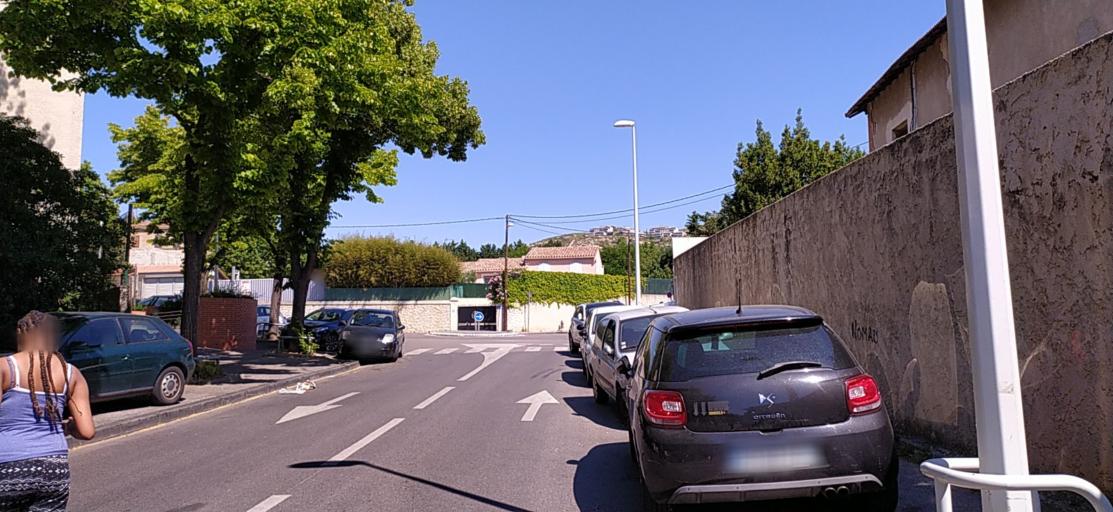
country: FR
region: Provence-Alpes-Cote d'Azur
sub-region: Departement des Bouches-du-Rhone
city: Marseille 16
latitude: 43.3603
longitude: 5.3354
